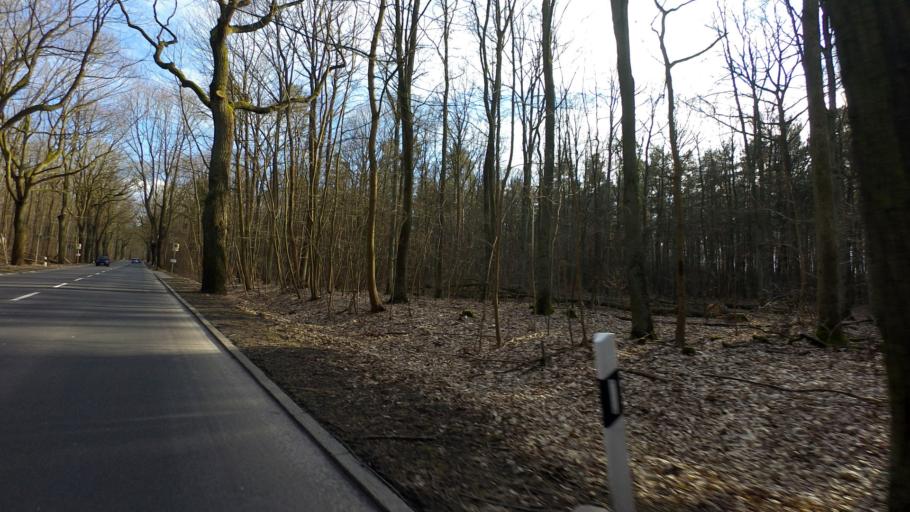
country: DE
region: Berlin
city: Frohnau
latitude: 52.6517
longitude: 13.2933
